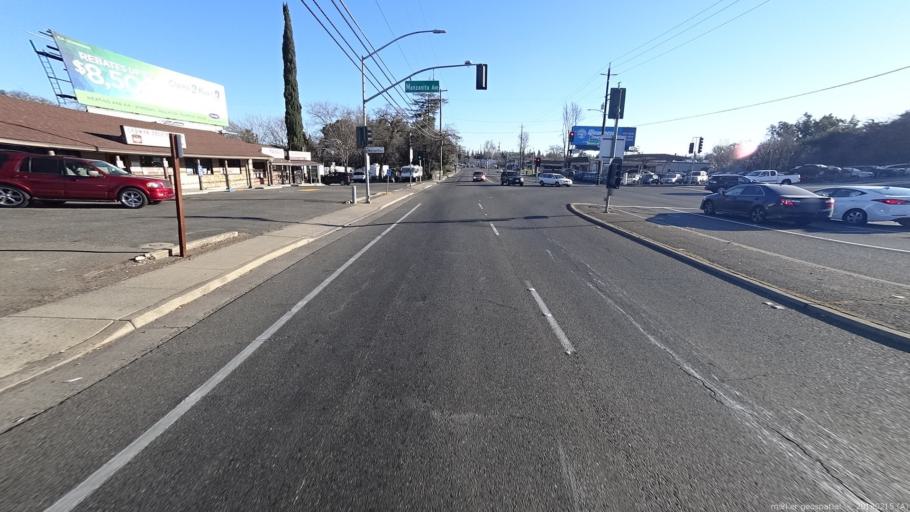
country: US
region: California
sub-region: Sacramento County
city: Foothill Farms
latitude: 38.6731
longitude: -121.3283
